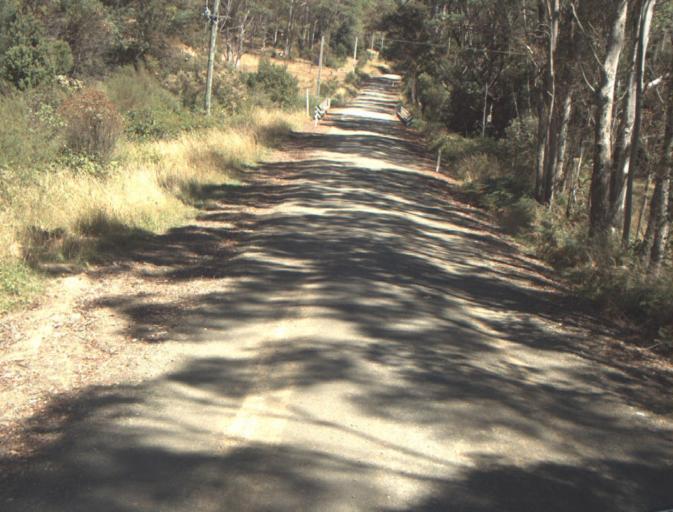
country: AU
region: Tasmania
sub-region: Launceston
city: Newstead
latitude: -41.3423
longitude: 147.3657
